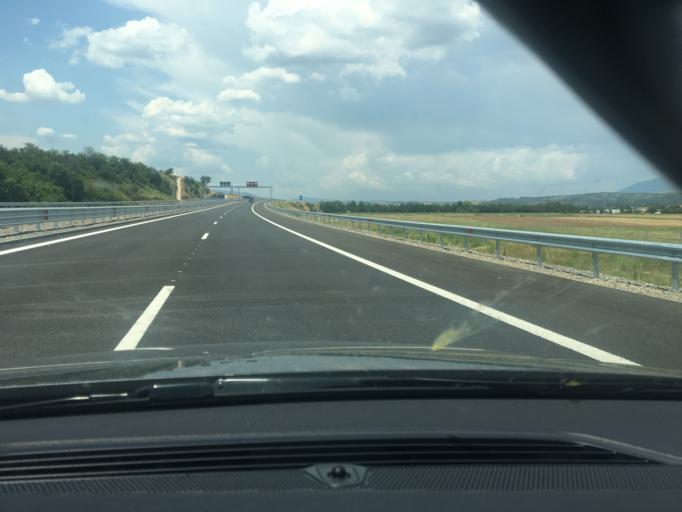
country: BG
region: Blagoevgrad
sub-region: Obshtina Blagoevgrad
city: Blagoevgrad
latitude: 41.9896
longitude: 23.0552
